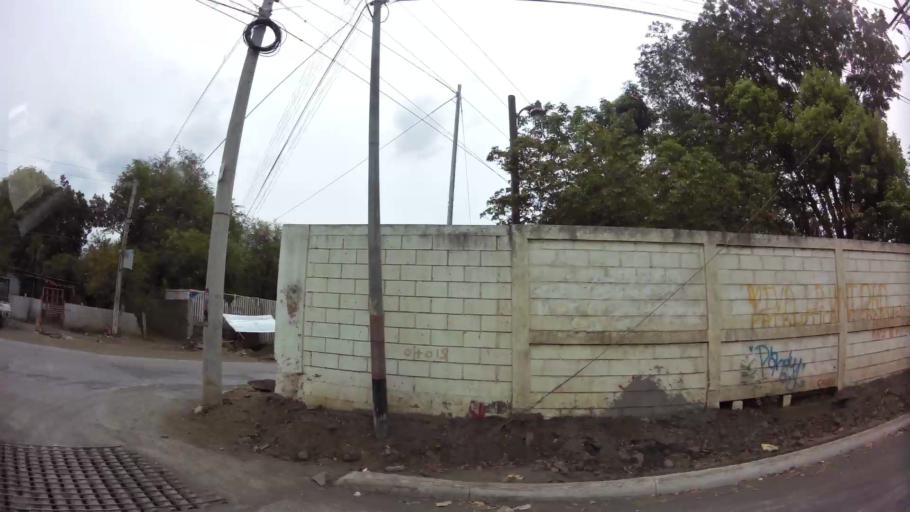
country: NI
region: Managua
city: Managua
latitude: 12.1204
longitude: -86.1695
